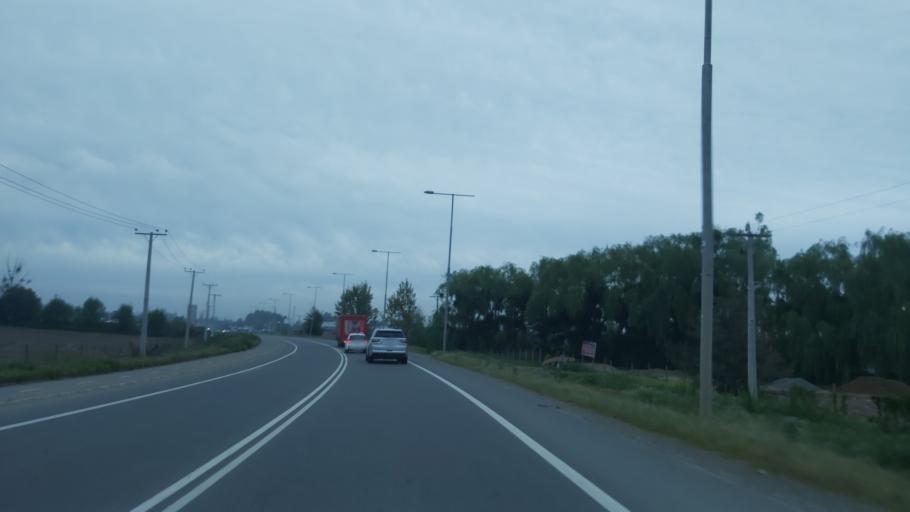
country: CL
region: Maule
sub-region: Provincia de Linares
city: Linares
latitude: -35.8317
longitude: -71.6187
